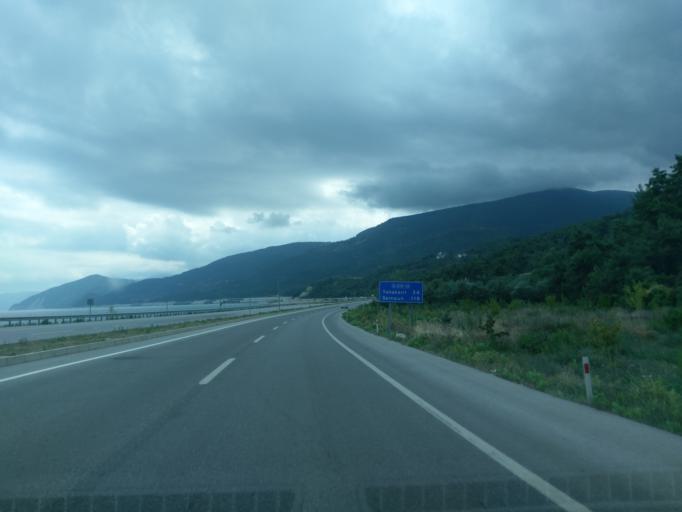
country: TR
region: Sinop
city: Gerze
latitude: 41.7808
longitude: 35.2018
